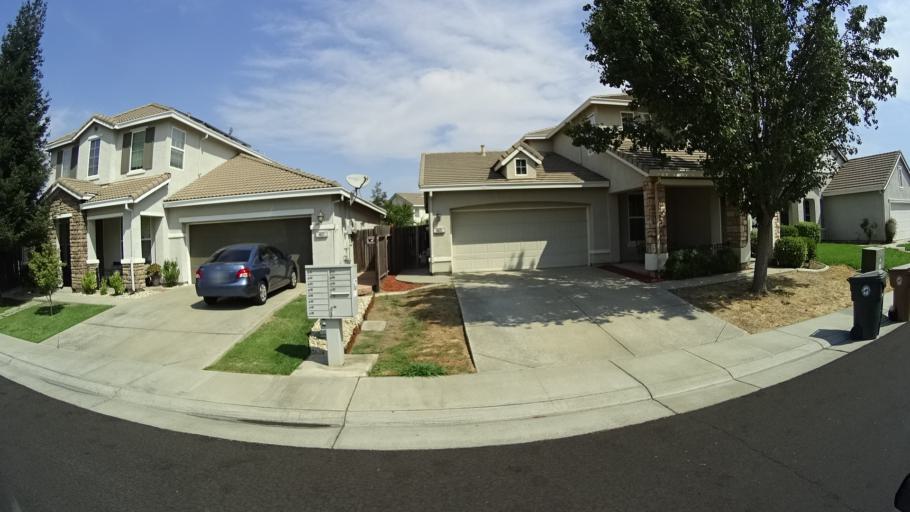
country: US
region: California
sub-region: Sacramento County
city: Laguna
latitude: 38.3861
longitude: -121.4501
